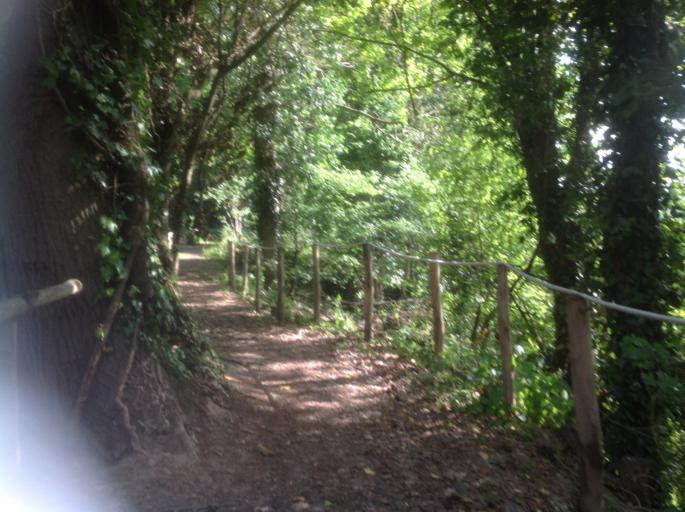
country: IT
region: Latium
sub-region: Provincia di Rieti
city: Colli sul Velino
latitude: 42.4752
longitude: 12.8057
